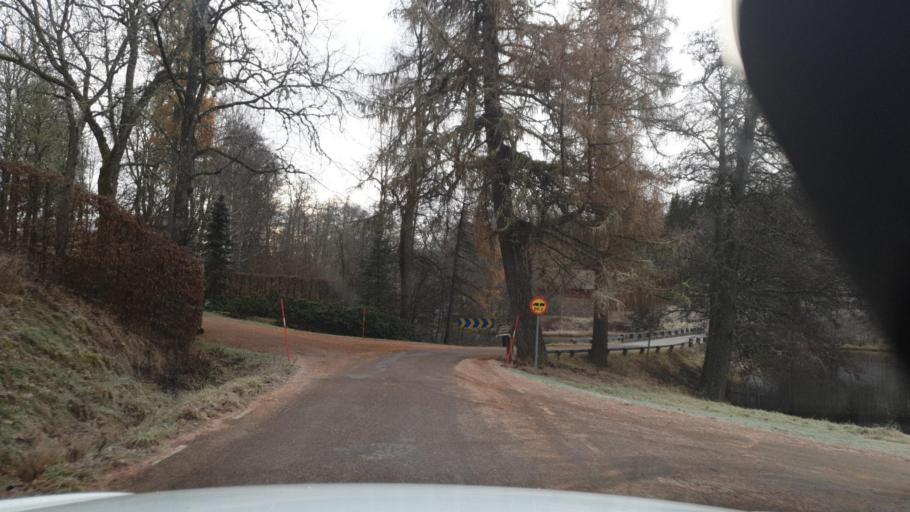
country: SE
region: Vaermland
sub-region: Sunne Kommun
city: Sunne
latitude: 59.6189
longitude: 12.9617
